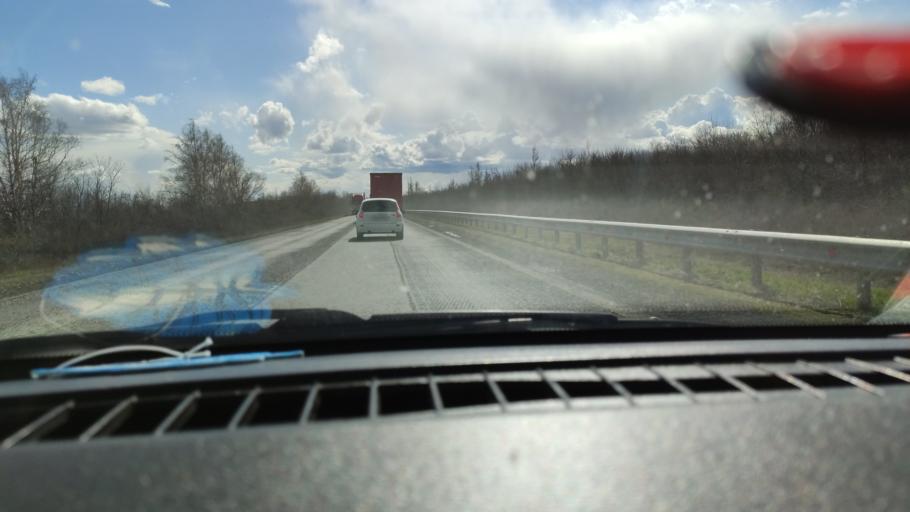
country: RU
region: Saratov
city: Dukhovnitskoye
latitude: 52.6728
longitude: 48.2234
